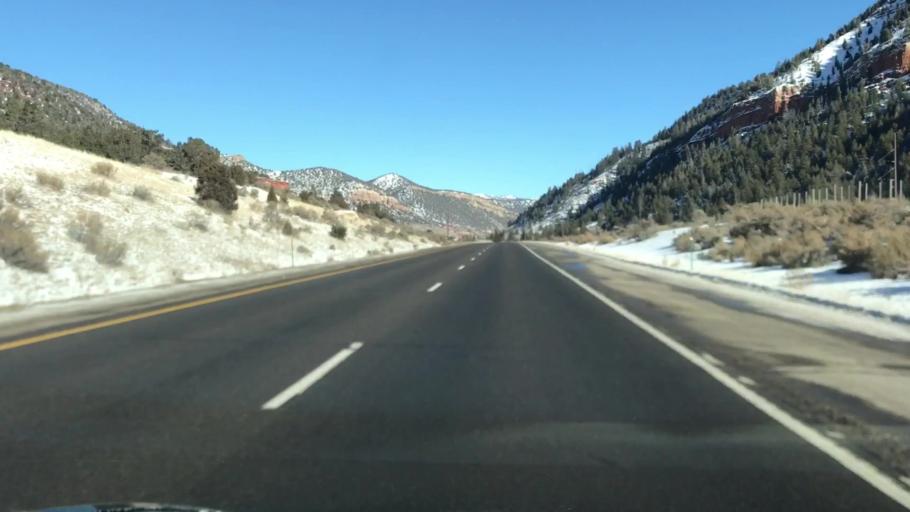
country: US
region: Colorado
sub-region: Eagle County
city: Eagle
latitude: 39.6980
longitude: -106.7374
